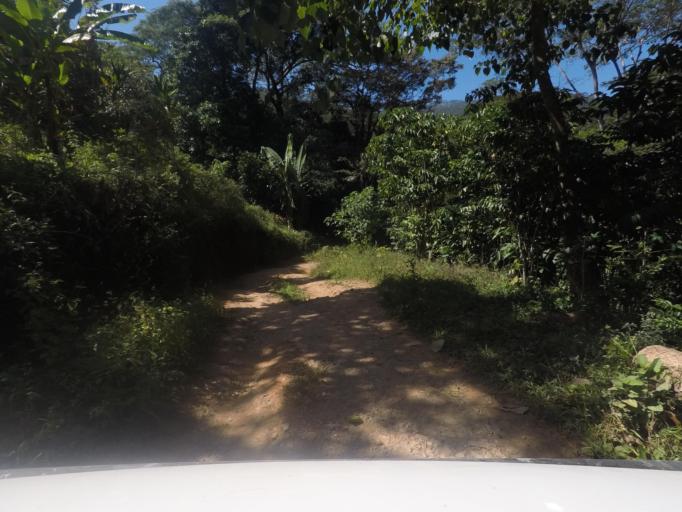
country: TL
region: Ermera
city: Gleno
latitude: -8.7202
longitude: 125.3166
